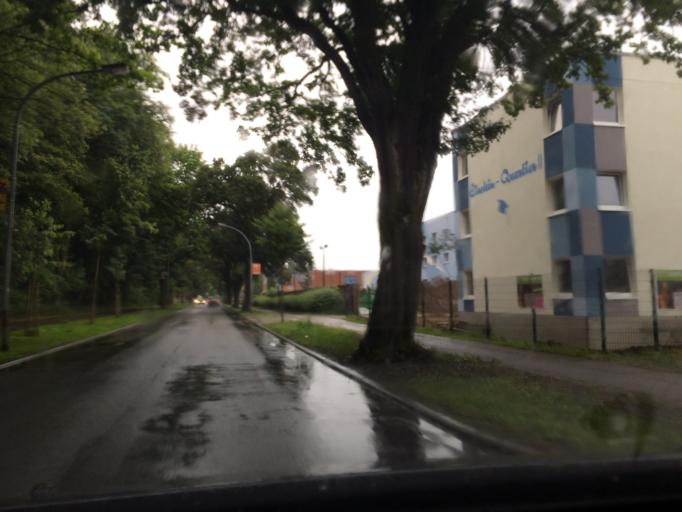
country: DE
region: Mecklenburg-Vorpommern
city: Stralsund
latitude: 54.3313
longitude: 13.0680
